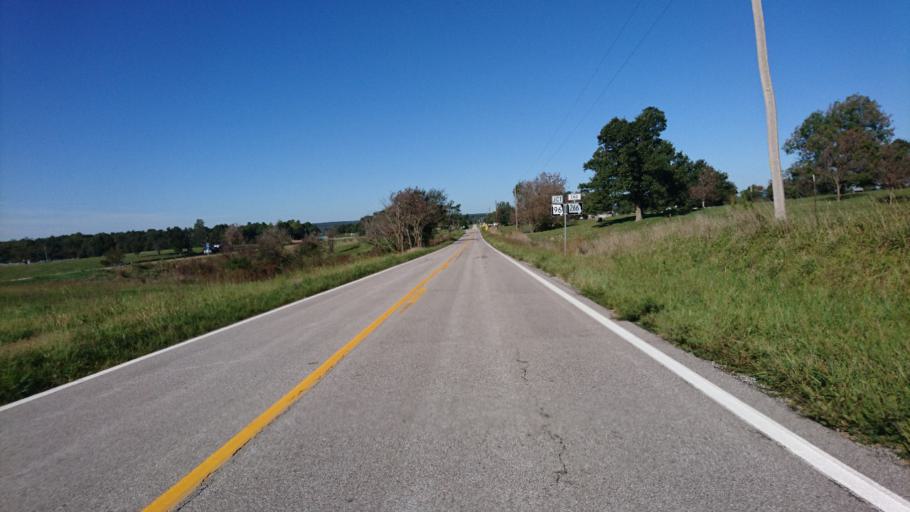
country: US
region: Missouri
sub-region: Greene County
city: Ash Grove
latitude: 37.1940
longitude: -93.6667
